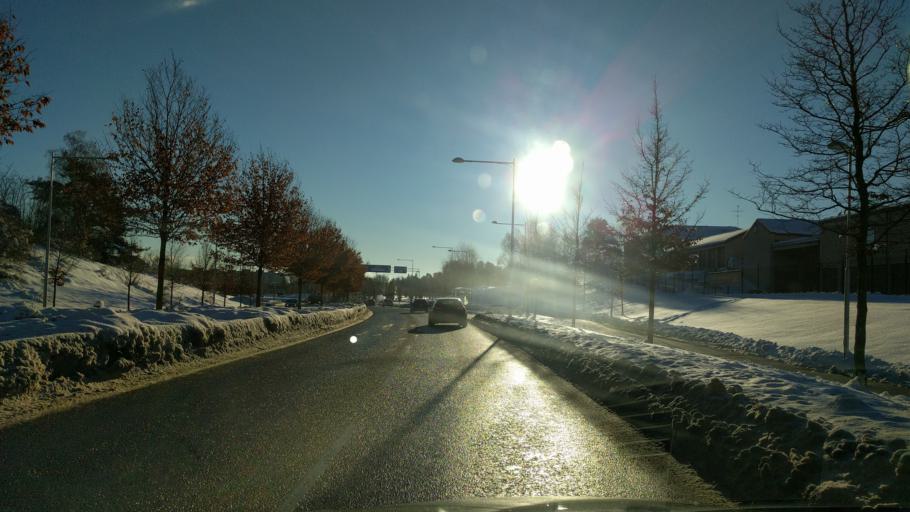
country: SE
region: Stockholm
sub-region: Taby Kommun
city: Taby
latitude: 59.4504
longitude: 18.0879
